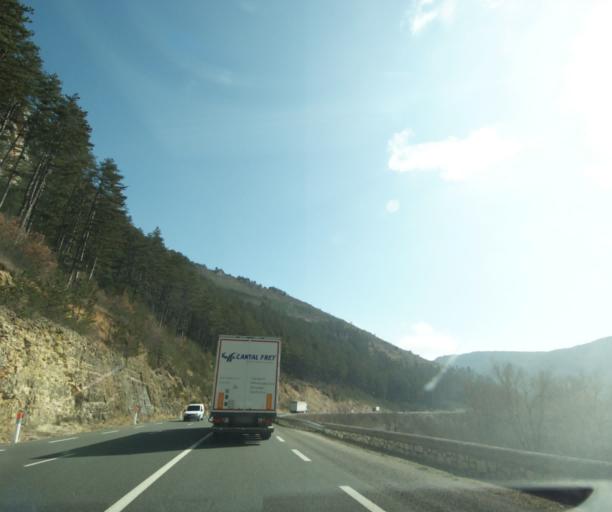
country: FR
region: Languedoc-Roussillon
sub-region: Departement de la Lozere
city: Chanac
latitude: 44.4864
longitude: 3.4221
